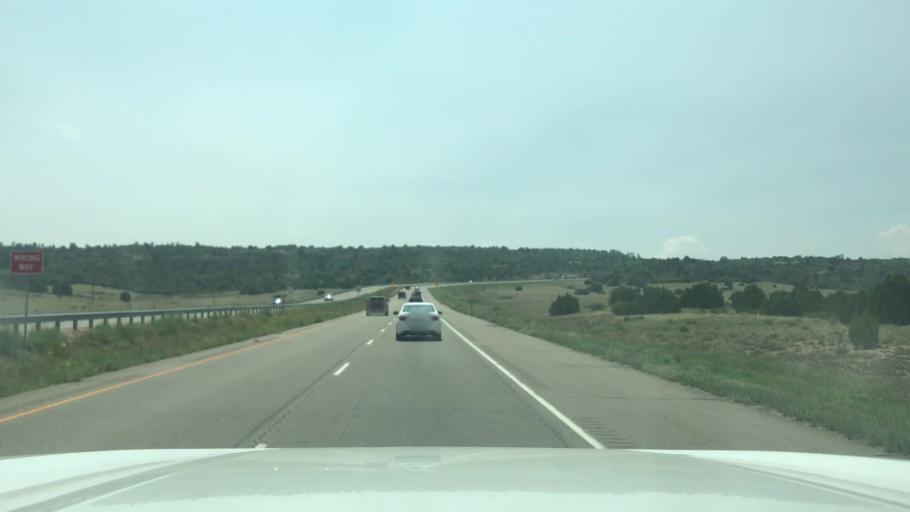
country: US
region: Colorado
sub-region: Pueblo County
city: Colorado City
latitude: 37.9455
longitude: -104.8042
